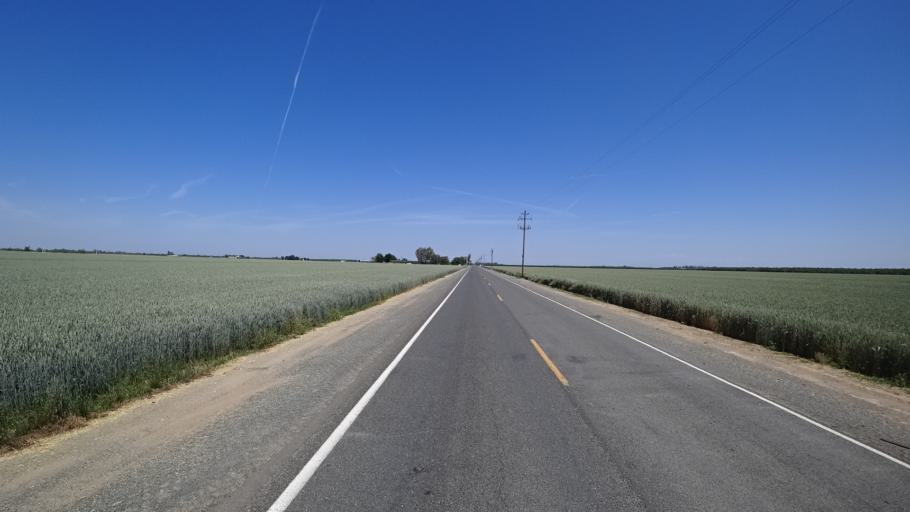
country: US
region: California
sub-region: Kings County
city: Armona
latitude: 36.2270
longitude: -119.7088
